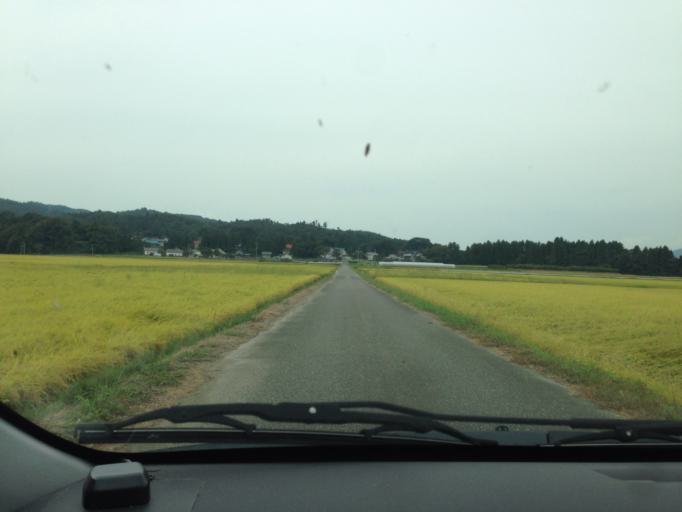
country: JP
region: Fukushima
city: Kitakata
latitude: 37.5993
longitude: 139.8215
